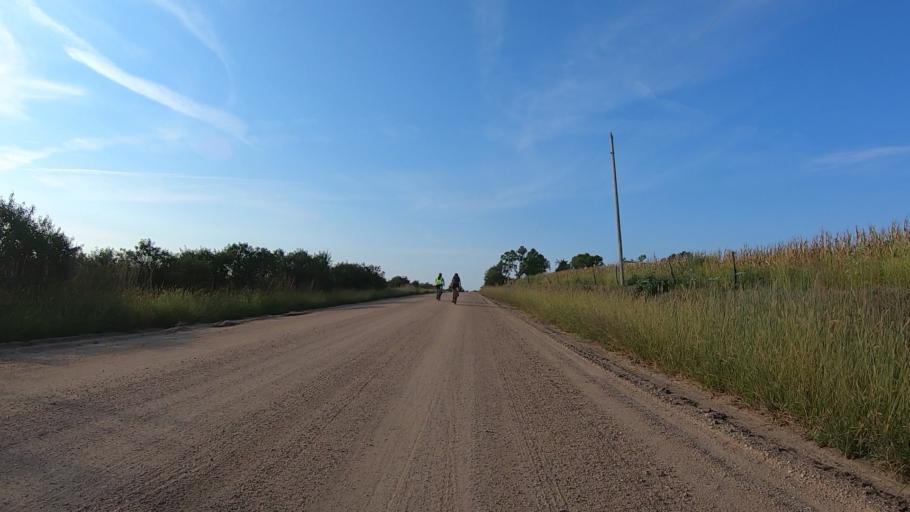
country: US
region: Kansas
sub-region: Marshall County
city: Blue Rapids
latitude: 39.6888
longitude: -96.7792
